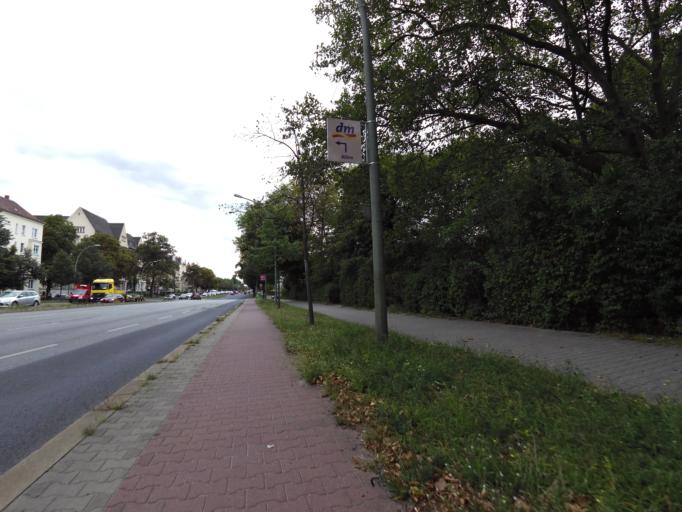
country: DE
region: Berlin
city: Baumschulenweg
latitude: 52.4673
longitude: 13.4943
